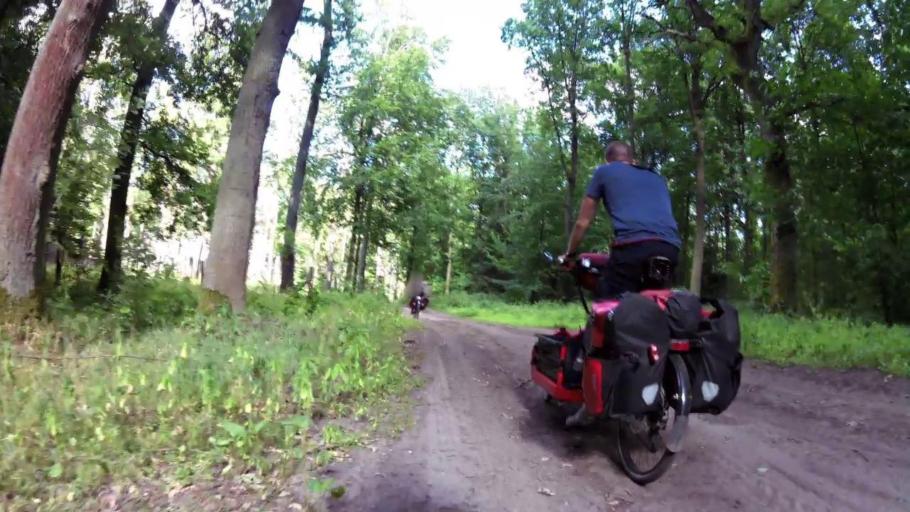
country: PL
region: West Pomeranian Voivodeship
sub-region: Powiat lobeski
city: Lobez
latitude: 53.6730
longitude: 15.7097
